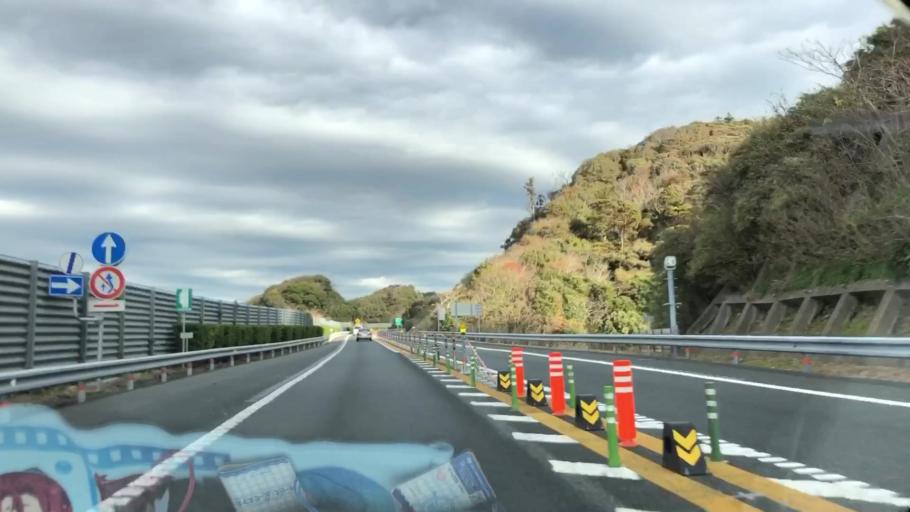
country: JP
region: Chiba
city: Tateyama
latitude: 35.0459
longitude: 139.8531
